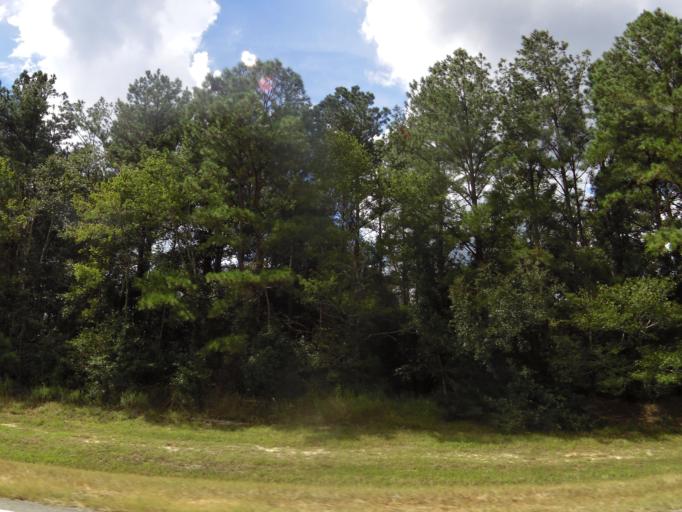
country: US
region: Georgia
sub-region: Brantley County
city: Nahunta
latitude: 31.1605
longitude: -81.9912
